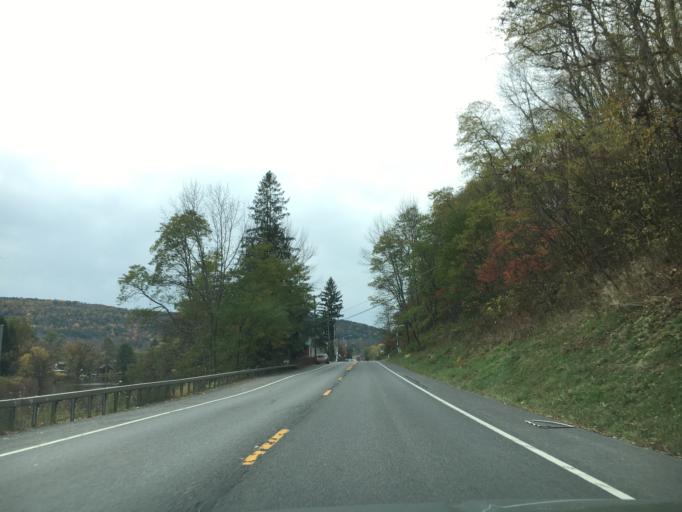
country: US
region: New York
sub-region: Otsego County
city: Oneonta
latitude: 42.5331
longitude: -74.9657
